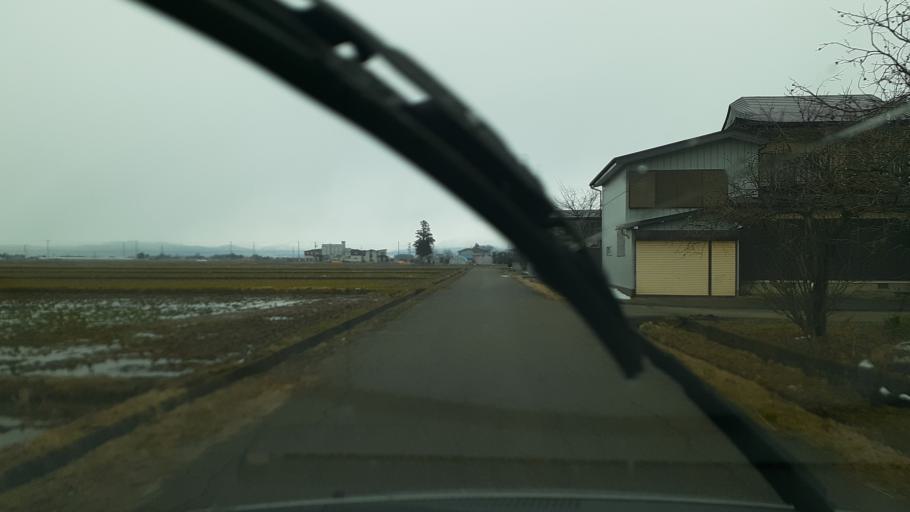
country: JP
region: Fukushima
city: Kitakata
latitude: 37.5605
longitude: 139.8831
